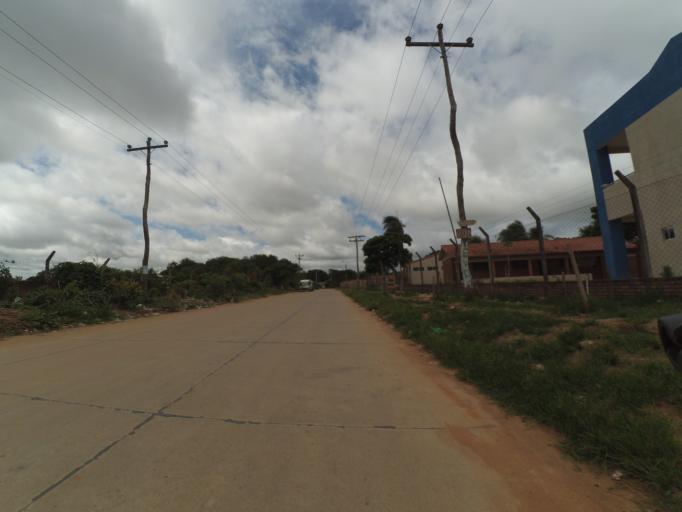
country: BO
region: Santa Cruz
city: Santa Cruz de la Sierra
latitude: -17.8732
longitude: -63.2339
